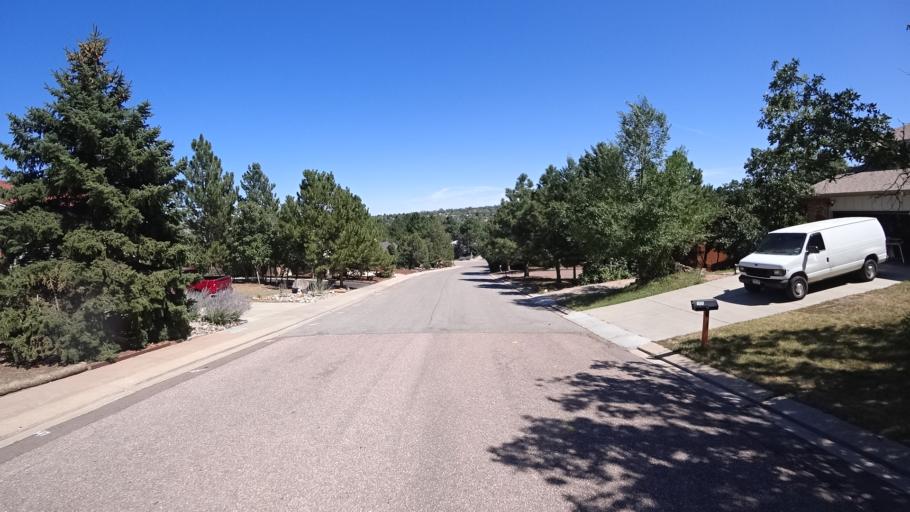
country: US
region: Colorado
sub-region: El Paso County
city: Colorado Springs
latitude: 38.9202
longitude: -104.7970
